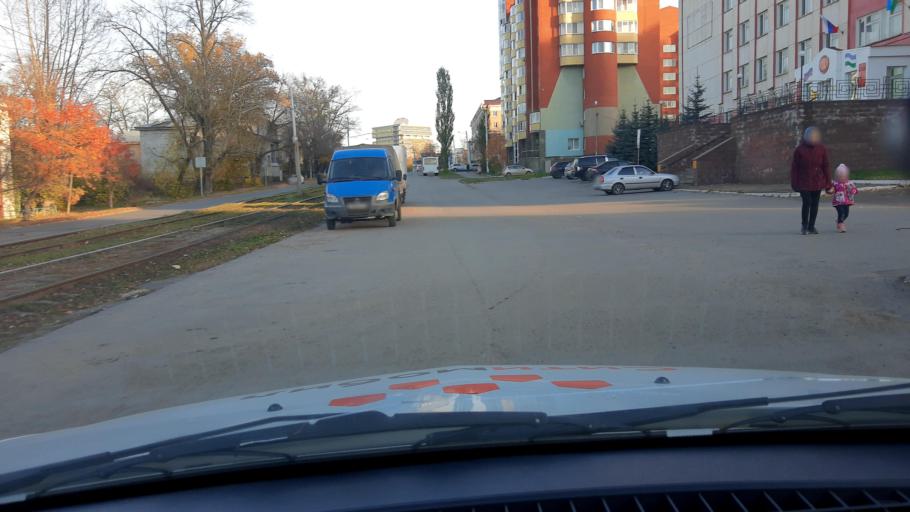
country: RU
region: Bashkortostan
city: Ufa
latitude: 54.8251
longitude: 56.0781
